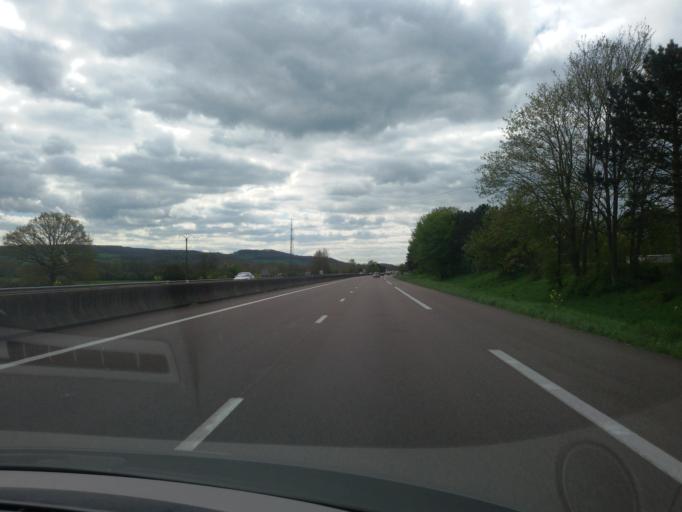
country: FR
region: Bourgogne
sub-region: Departement de la Cote-d'Or
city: Pouilly-en-Auxois
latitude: 47.3174
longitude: 4.4945
